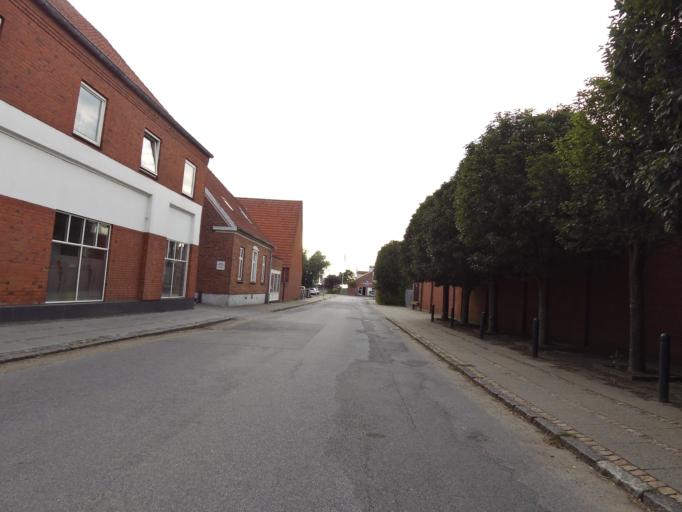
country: DK
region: South Denmark
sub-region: Esbjerg Kommune
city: Ribe
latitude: 55.3305
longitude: 8.7654
